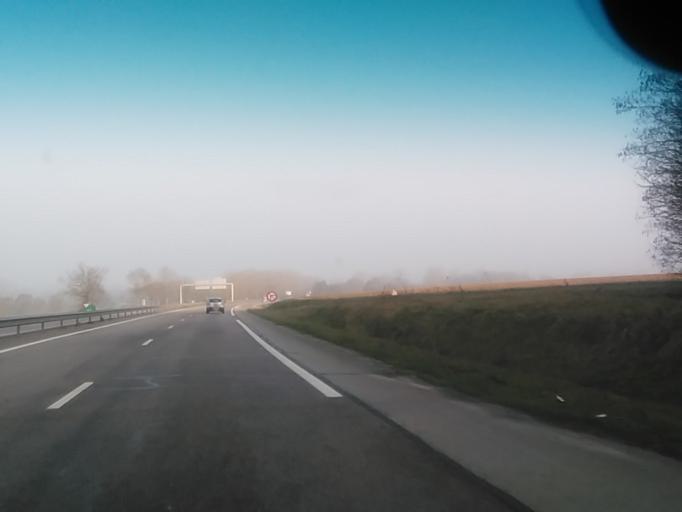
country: FR
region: Lower Normandy
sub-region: Departement du Calvados
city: Potigny
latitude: 48.9495
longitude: -0.2200
